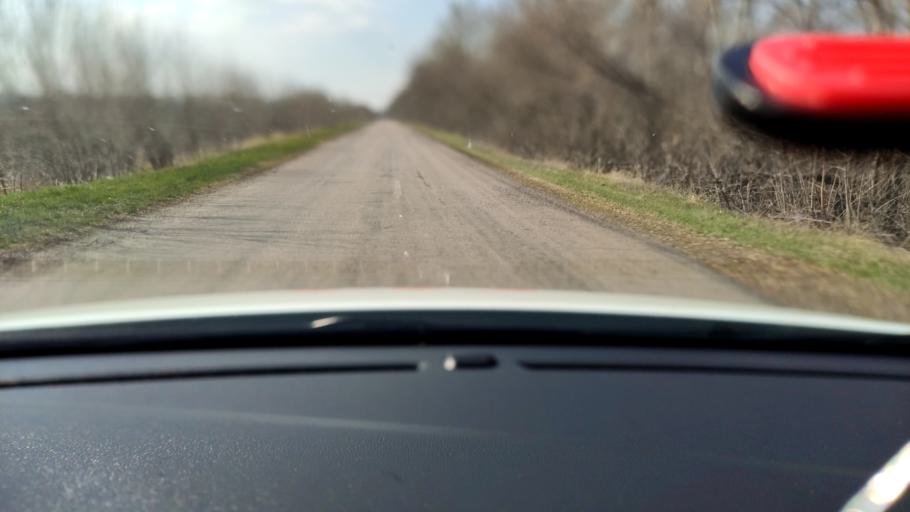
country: RU
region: Voronezj
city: Uryv-Pokrovka
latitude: 51.1437
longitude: 39.0686
